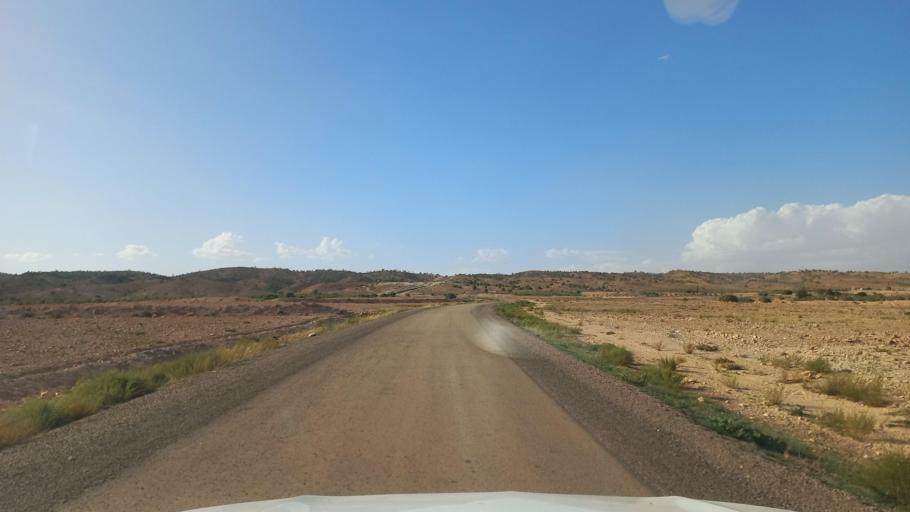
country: TN
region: Al Qasrayn
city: Sbiba
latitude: 35.3506
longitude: 8.9872
